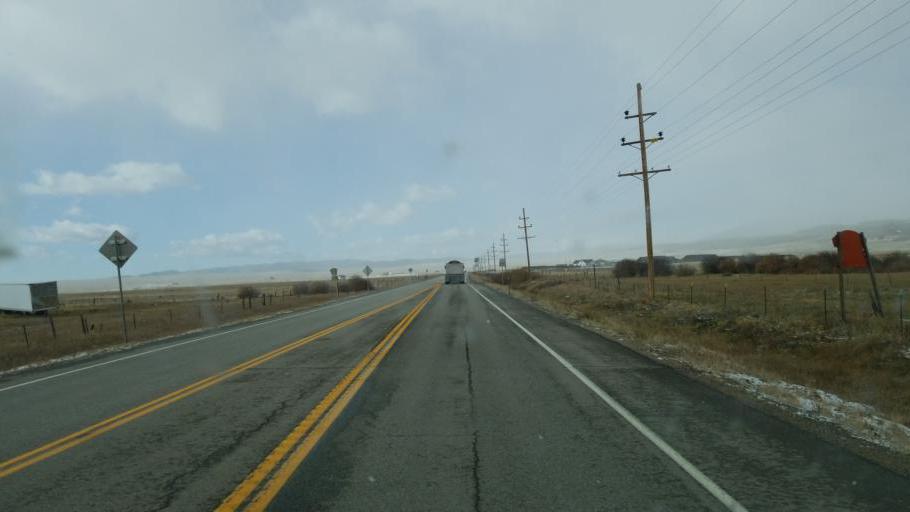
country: US
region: Colorado
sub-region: Park County
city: Fairplay
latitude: 39.3765
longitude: -105.8015
